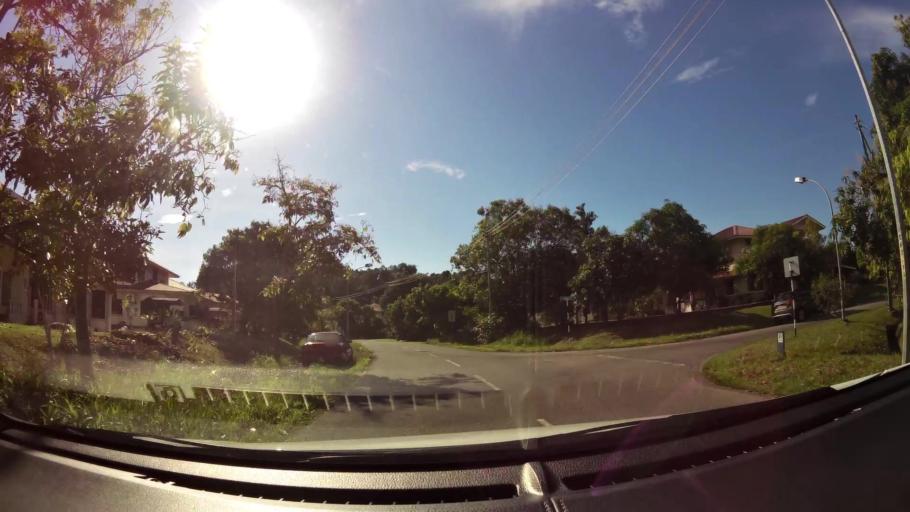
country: BN
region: Brunei and Muara
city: Bandar Seri Begawan
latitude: 4.9664
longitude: 114.9615
